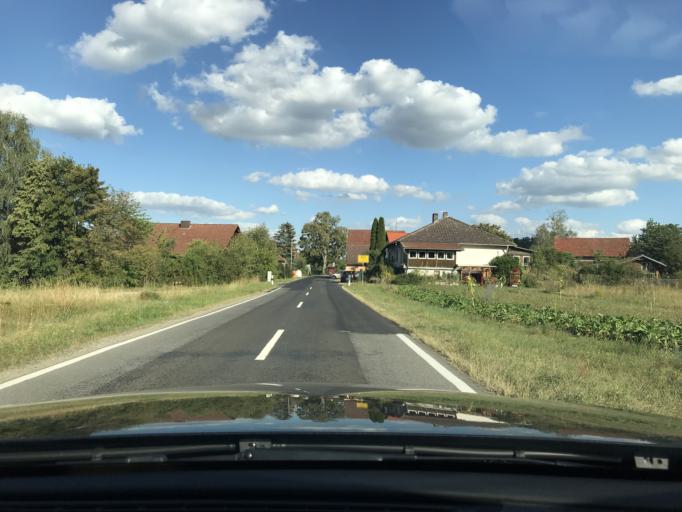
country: DE
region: Bavaria
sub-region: Regierungsbezirk Unterfranken
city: Burgpreppach
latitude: 50.0768
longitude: 10.6580
